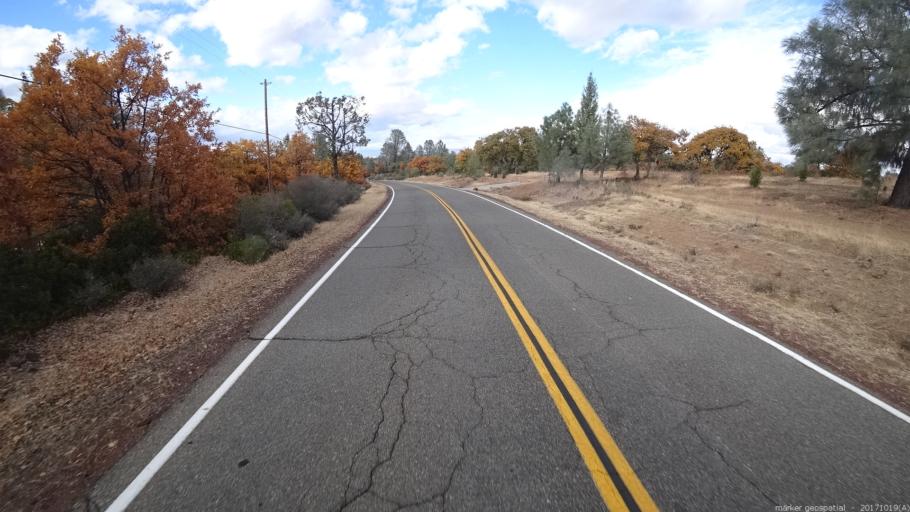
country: US
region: California
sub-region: Shasta County
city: Burney
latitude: 40.9648
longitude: -121.4353
